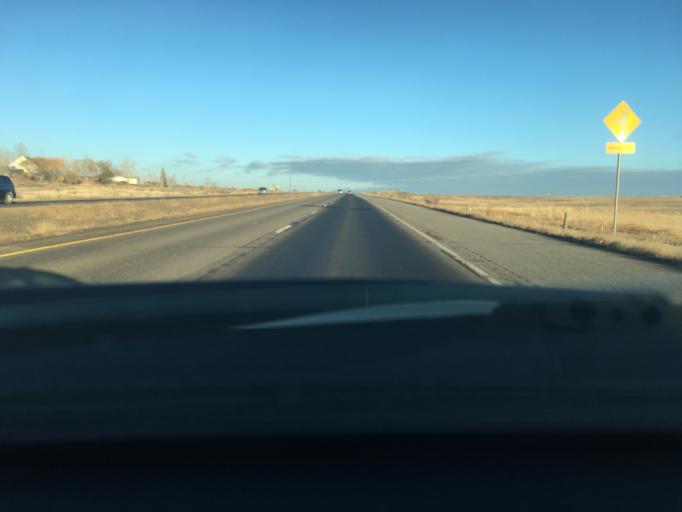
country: US
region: Colorado
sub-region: Montrose County
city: Olathe
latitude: 38.5409
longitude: -107.9422
